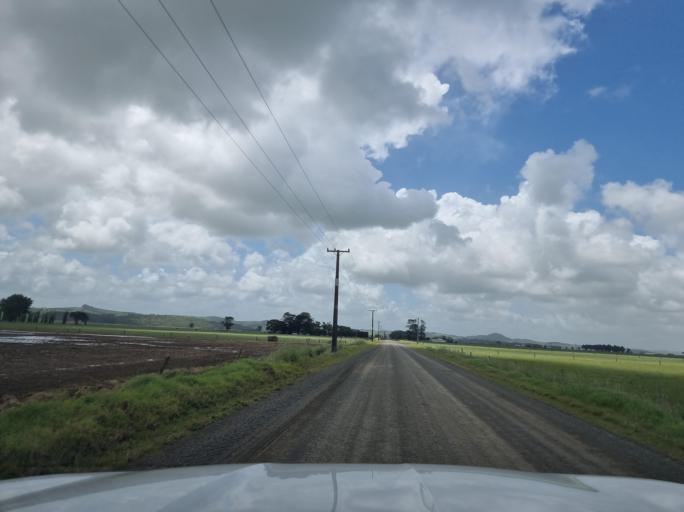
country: NZ
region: Northland
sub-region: Kaipara District
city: Dargaville
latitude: -36.0865
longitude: 174.0146
